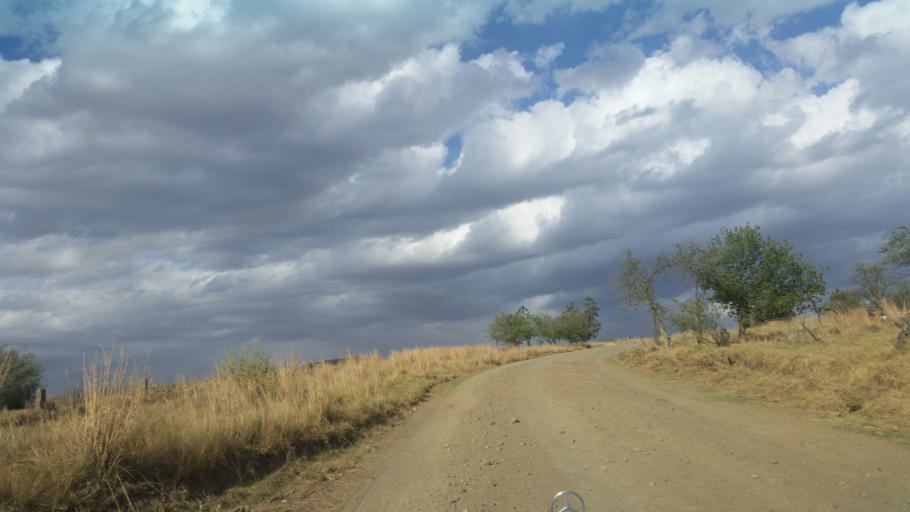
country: ZA
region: Orange Free State
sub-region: Thabo Mofutsanyana District Municipality
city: Phuthaditjhaba
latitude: -28.3709
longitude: 28.5972
